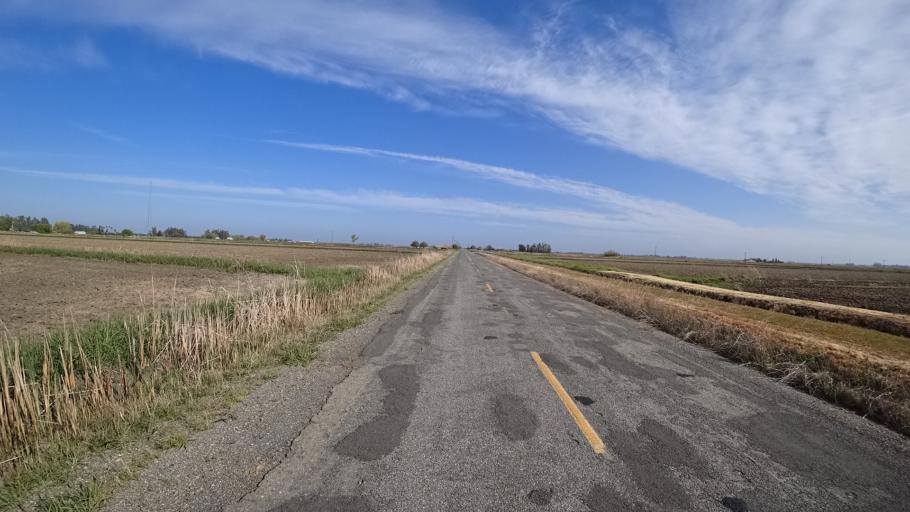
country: US
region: California
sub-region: Glenn County
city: Hamilton City
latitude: 39.5923
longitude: -122.0464
